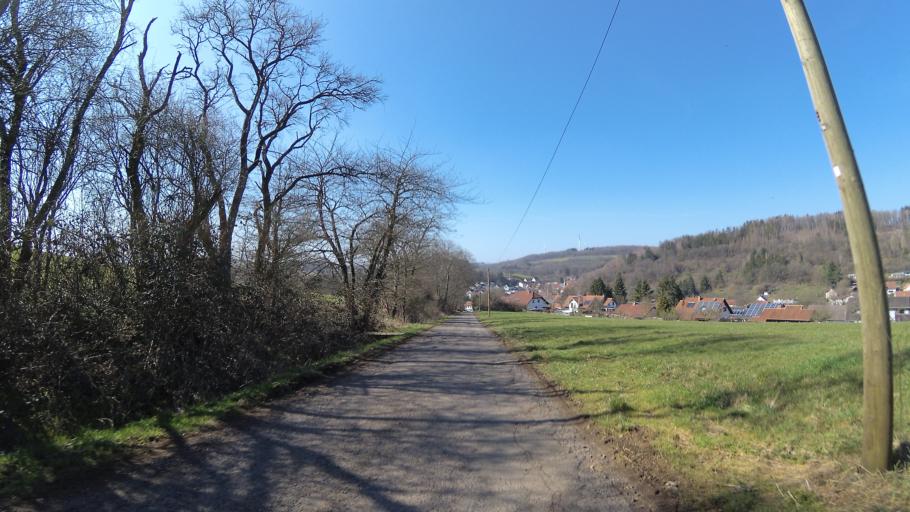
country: DE
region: Saarland
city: Marpingen
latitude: 49.4315
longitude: 7.0381
